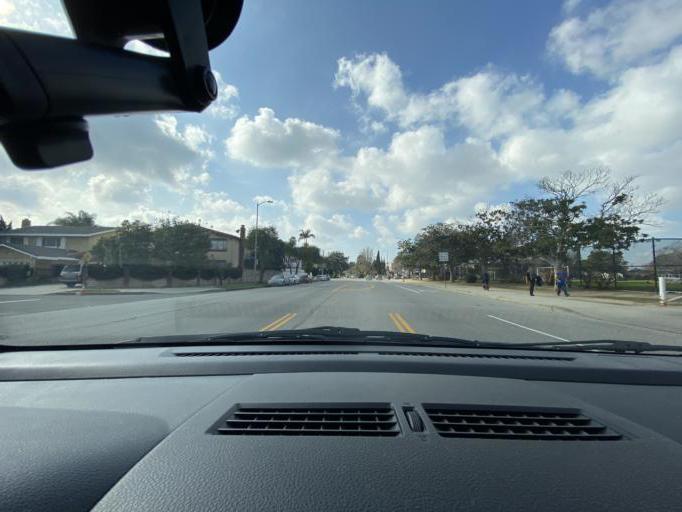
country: US
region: California
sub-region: Los Angeles County
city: Culver City
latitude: 34.0163
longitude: -118.4293
